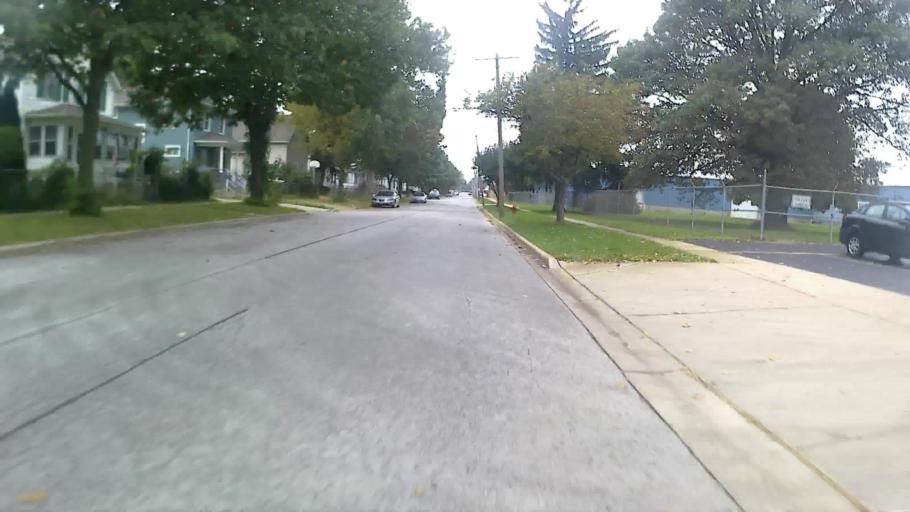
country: US
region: Illinois
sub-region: Kane County
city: Aurora
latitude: 41.7546
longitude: -88.3279
